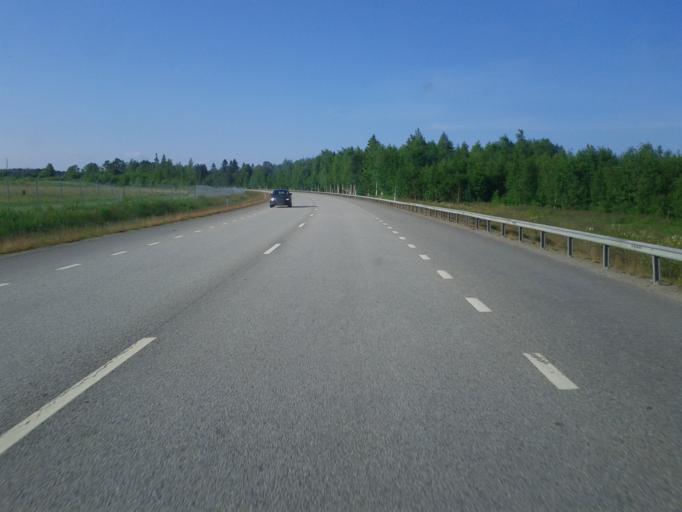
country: SE
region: Vaesterbotten
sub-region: Umea Kommun
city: Umea
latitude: 63.7822
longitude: 20.3040
